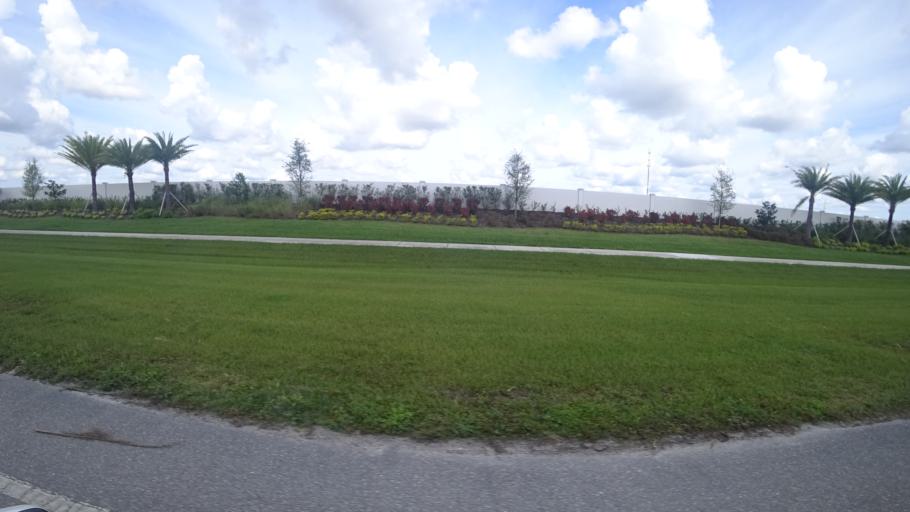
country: US
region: Florida
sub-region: Sarasota County
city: The Meadows
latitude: 27.3867
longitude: -82.3557
